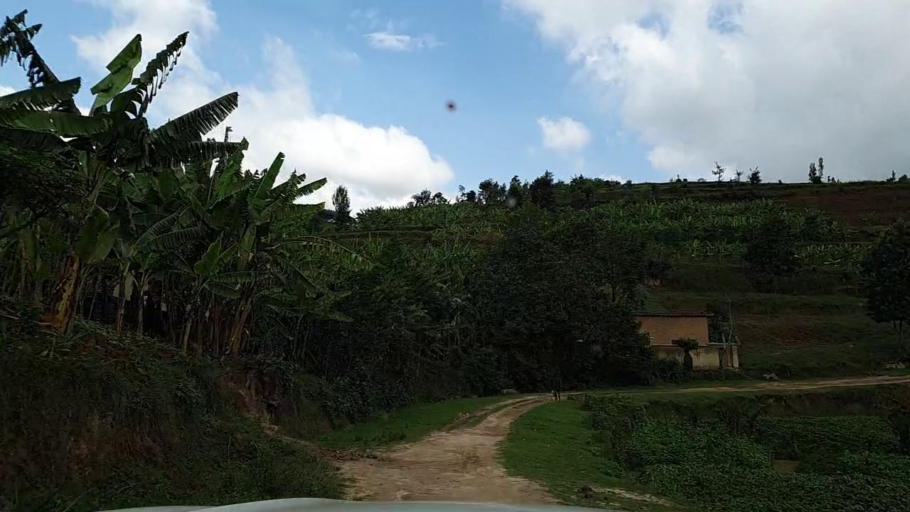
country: RW
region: Southern Province
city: Gikongoro
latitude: -2.3920
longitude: 29.5515
